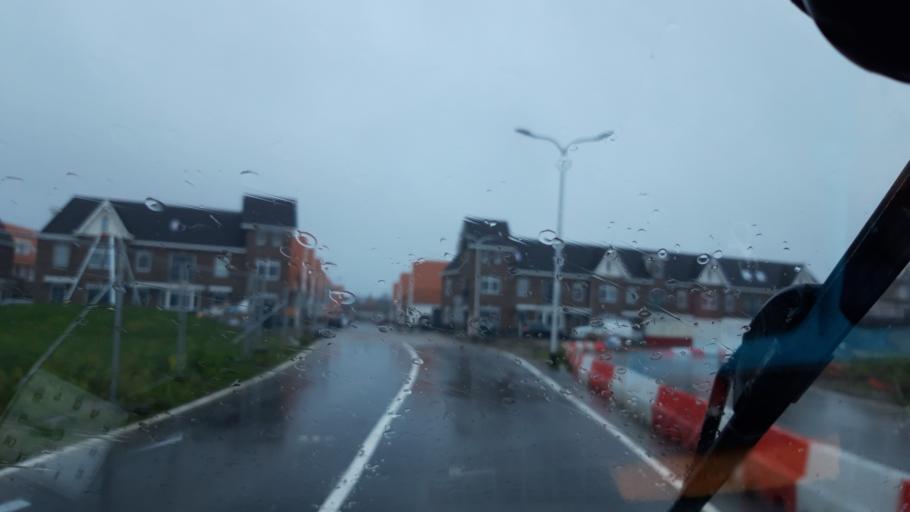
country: NL
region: South Holland
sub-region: Gemeente Westland
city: Poeldijk
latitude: 52.0281
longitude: 4.2235
